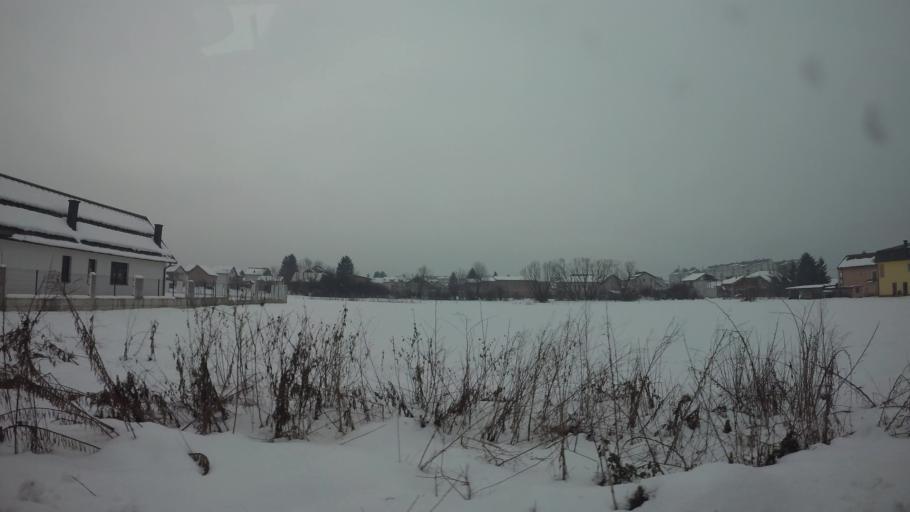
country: BA
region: Federation of Bosnia and Herzegovina
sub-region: Kanton Sarajevo
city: Sarajevo
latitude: 43.8420
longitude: 18.3031
